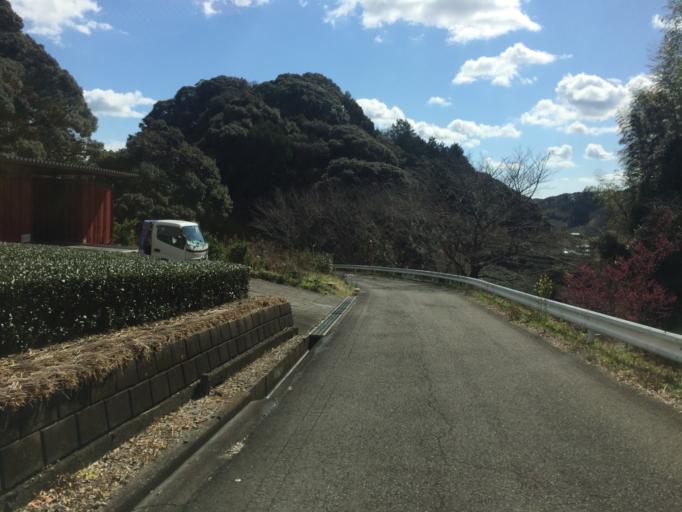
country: JP
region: Shizuoka
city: Shimada
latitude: 34.7684
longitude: 138.1956
